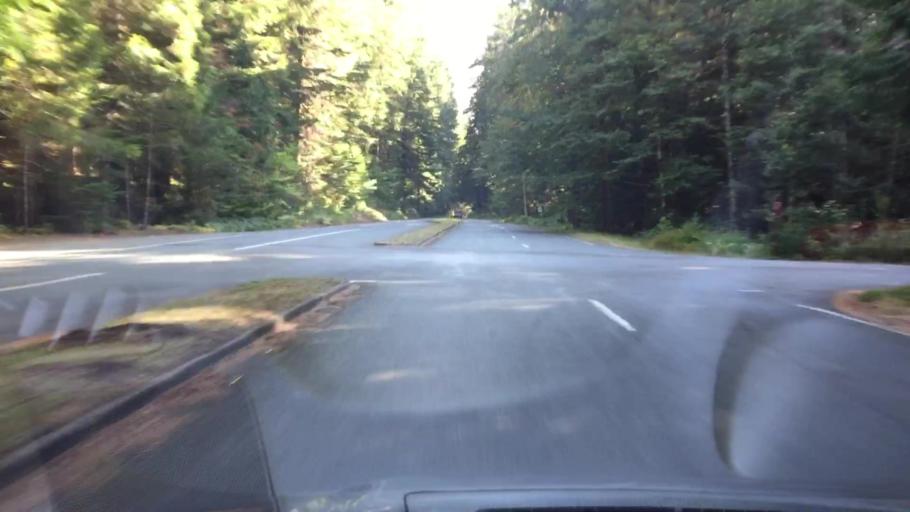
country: US
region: Washington
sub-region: Pierce County
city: Buckley
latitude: 46.7325
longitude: -121.5687
